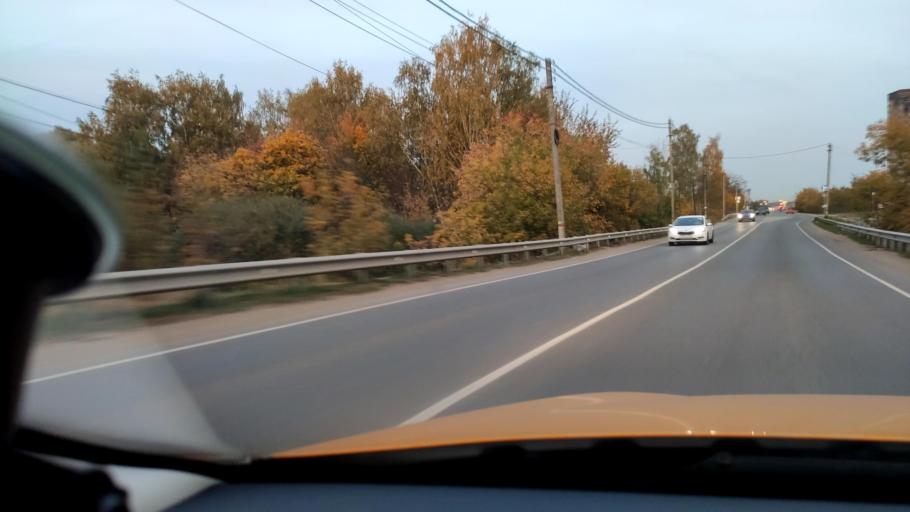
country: RU
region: Moskovskaya
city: Pirogovskiy
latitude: 55.9729
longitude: 37.7335
